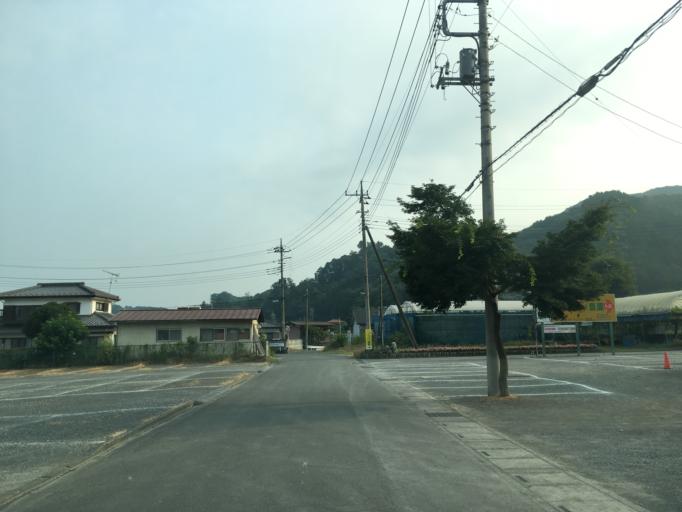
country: JP
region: Saitama
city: Chichibu
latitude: 35.9812
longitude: 139.1128
